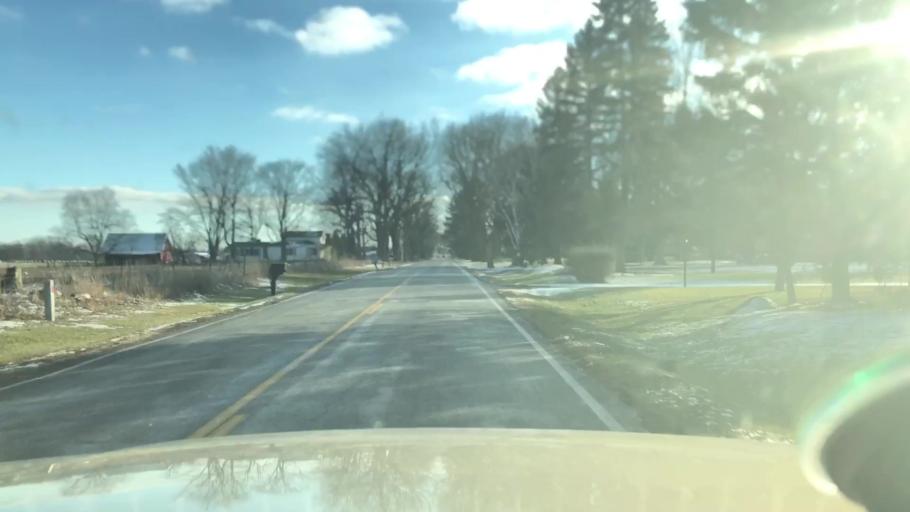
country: US
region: Michigan
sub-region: Jackson County
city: Vandercook Lake
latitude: 42.1743
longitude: -84.4521
